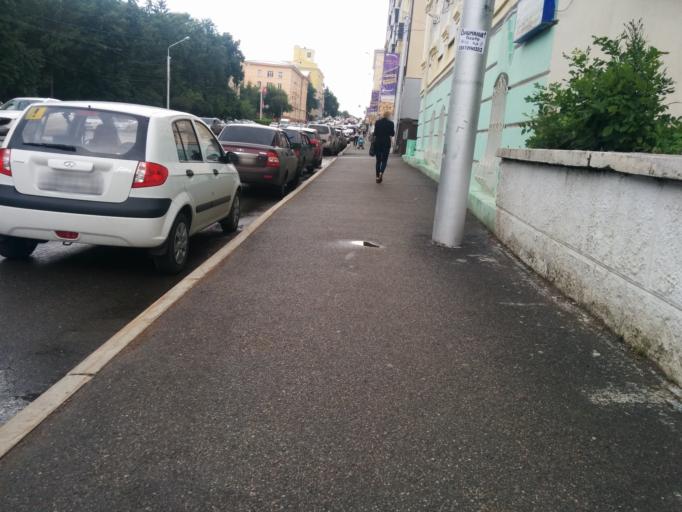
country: RU
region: Bashkortostan
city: Ufa
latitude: 54.7254
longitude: 55.9524
